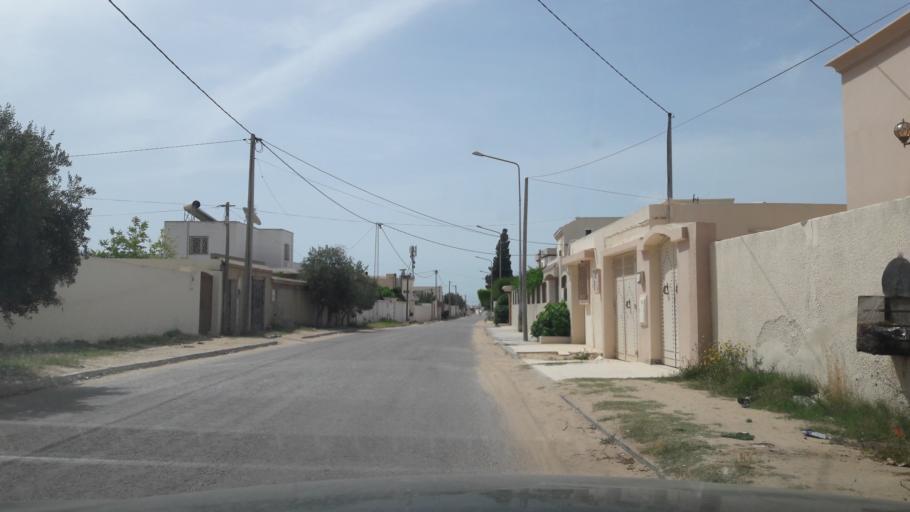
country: TN
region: Safaqis
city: Al Qarmadah
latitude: 34.7958
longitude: 10.7529
